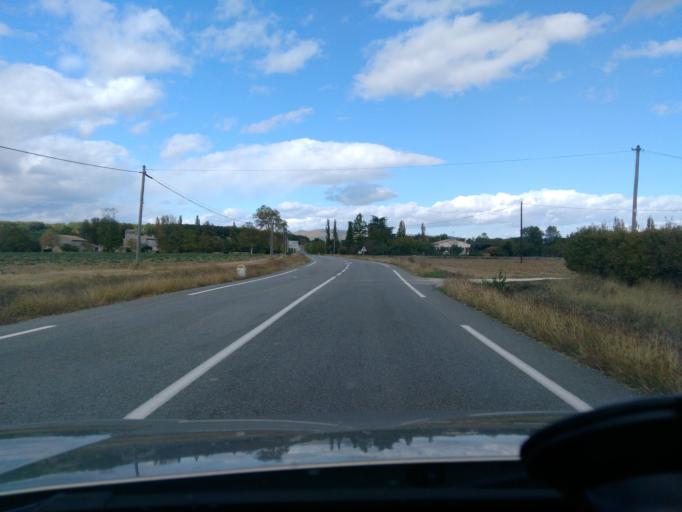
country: FR
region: Rhone-Alpes
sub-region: Departement de la Drome
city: Montboucher-sur-Jabron
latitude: 44.5557
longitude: 4.8517
